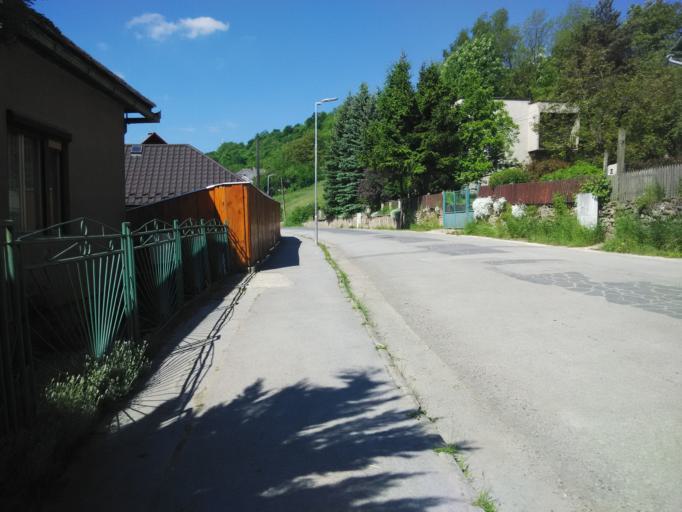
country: SK
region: Kosicky
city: Dobsina
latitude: 48.8217
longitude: 20.3558
